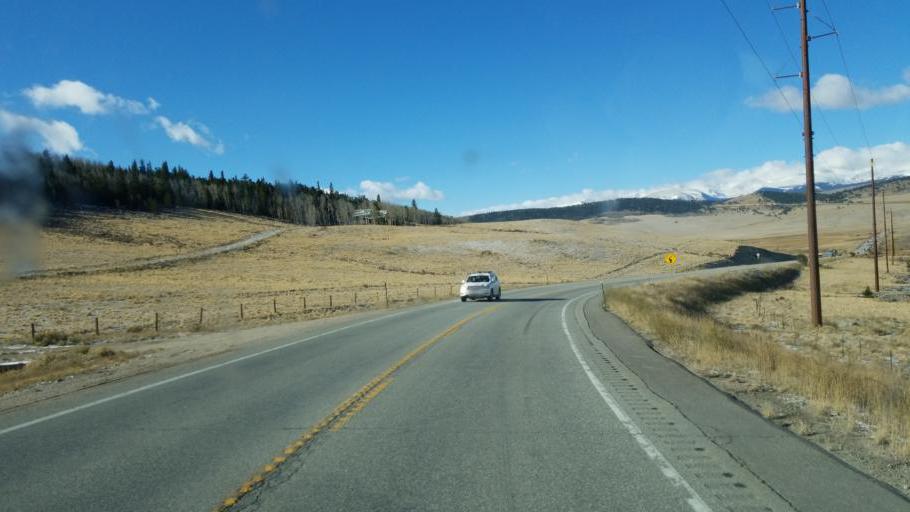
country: US
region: Colorado
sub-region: Park County
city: Fairplay
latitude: 39.2797
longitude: -105.9160
